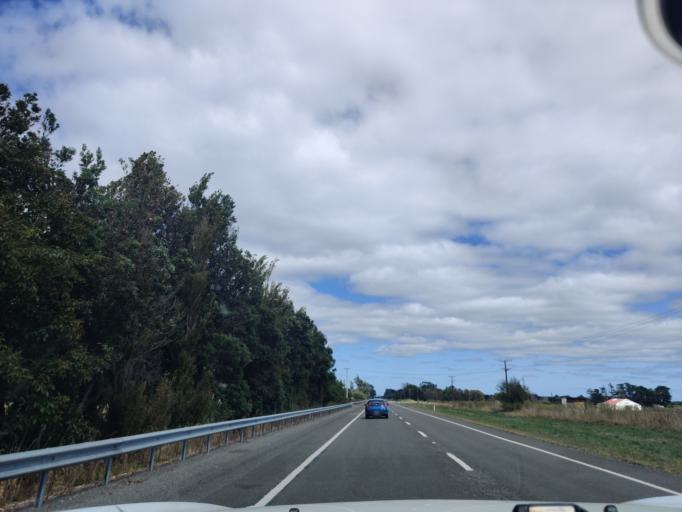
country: NZ
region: Manawatu-Wanganui
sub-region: Palmerston North City
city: Palmerston North
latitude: -40.3929
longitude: 175.5223
